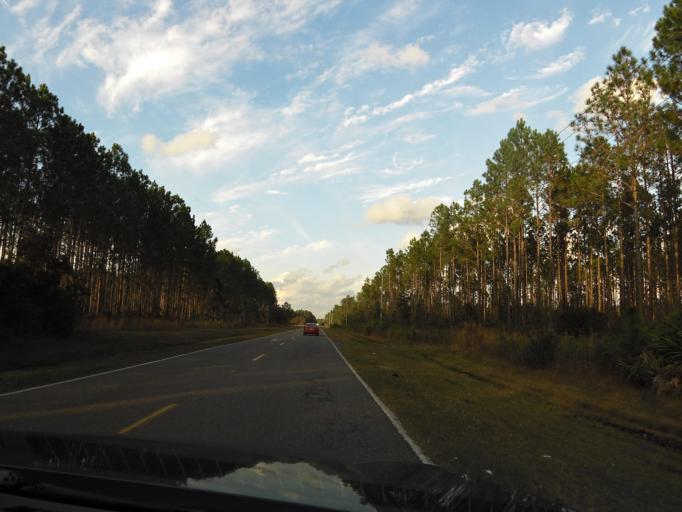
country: US
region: Florida
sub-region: Duval County
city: Baldwin
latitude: 30.1659
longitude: -81.9977
